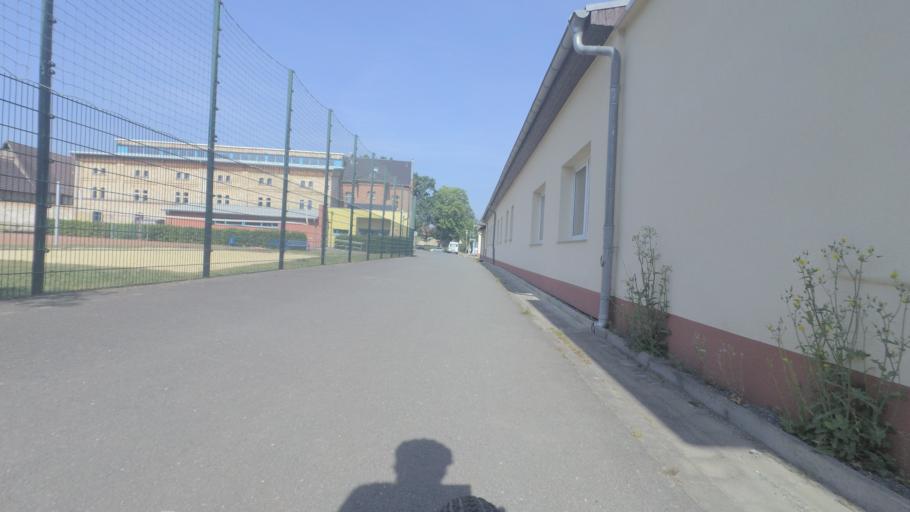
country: DE
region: Saxony-Anhalt
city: Hoym
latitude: 51.7844
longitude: 11.3166
